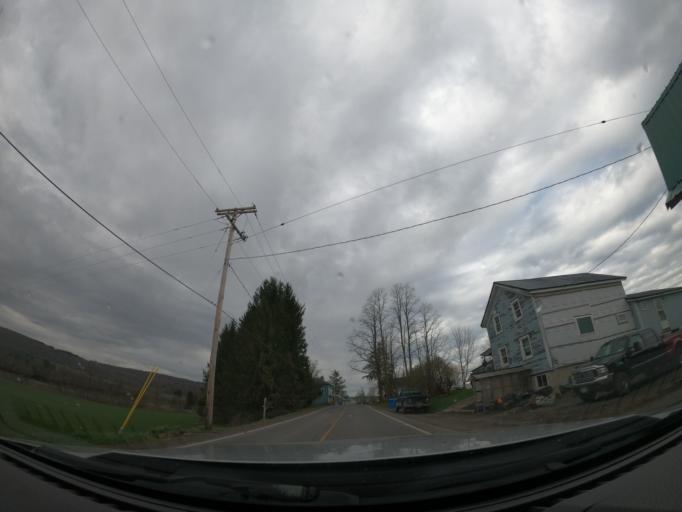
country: US
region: New York
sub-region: Madison County
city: Cazenovia
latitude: 42.8126
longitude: -75.8286
